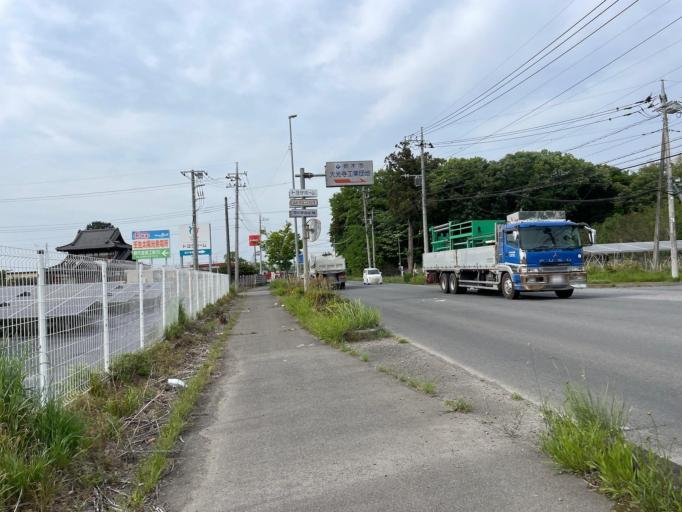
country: JP
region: Tochigi
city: Mibu
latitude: 36.4040
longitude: 139.8037
